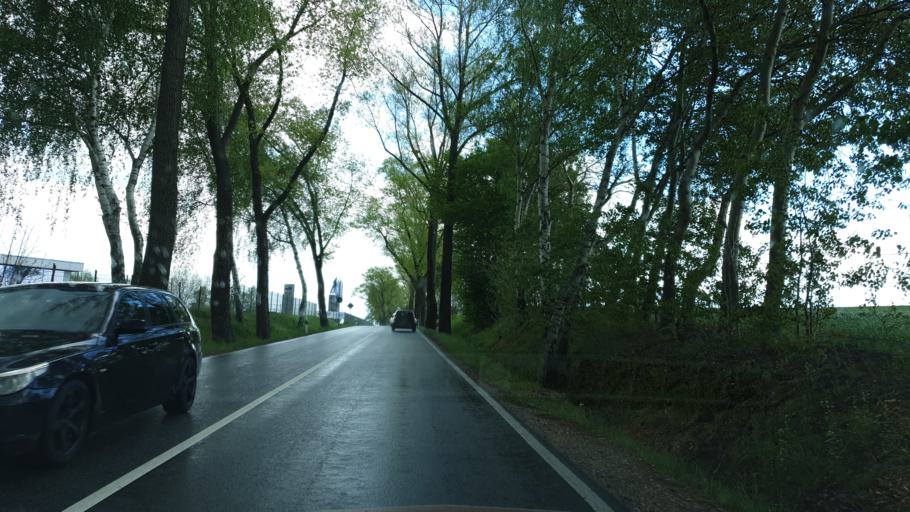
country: DE
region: Saxony
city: Neukirchen
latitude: 50.8064
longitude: 12.8271
